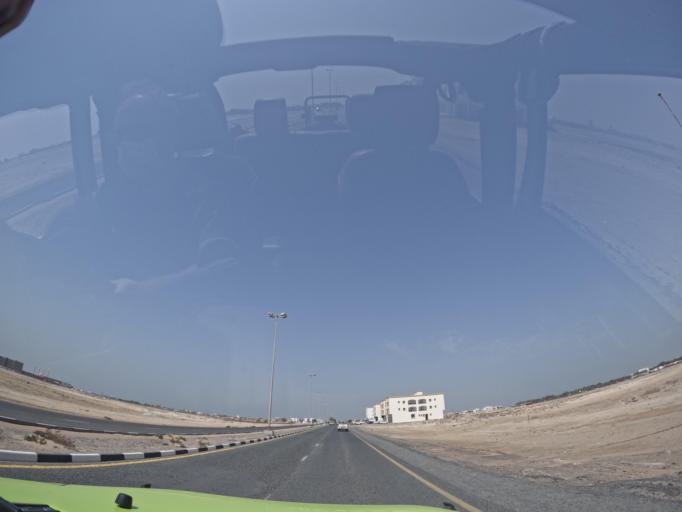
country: AE
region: Umm al Qaywayn
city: Umm al Qaywayn
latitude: 25.5184
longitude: 55.5551
